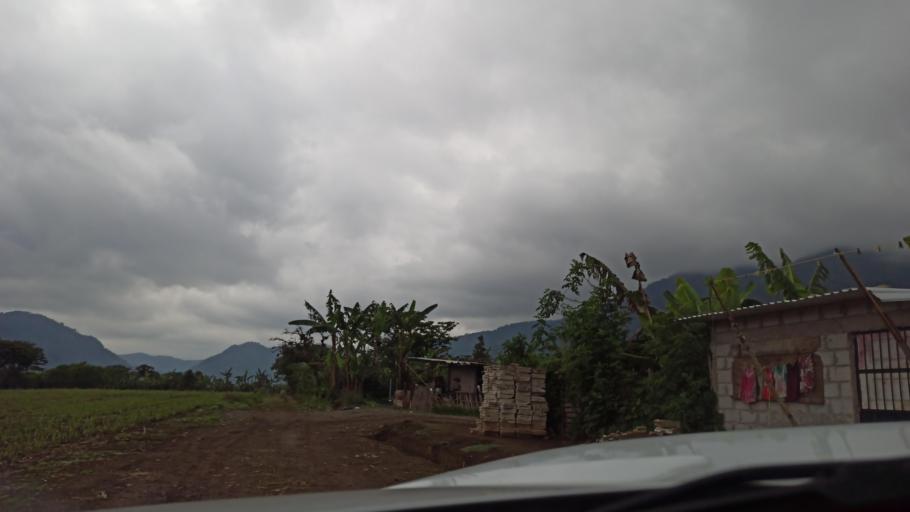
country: MX
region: Veracruz
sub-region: Fortin
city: Santa Lucia Potrerillo
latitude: 18.9664
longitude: -97.0295
